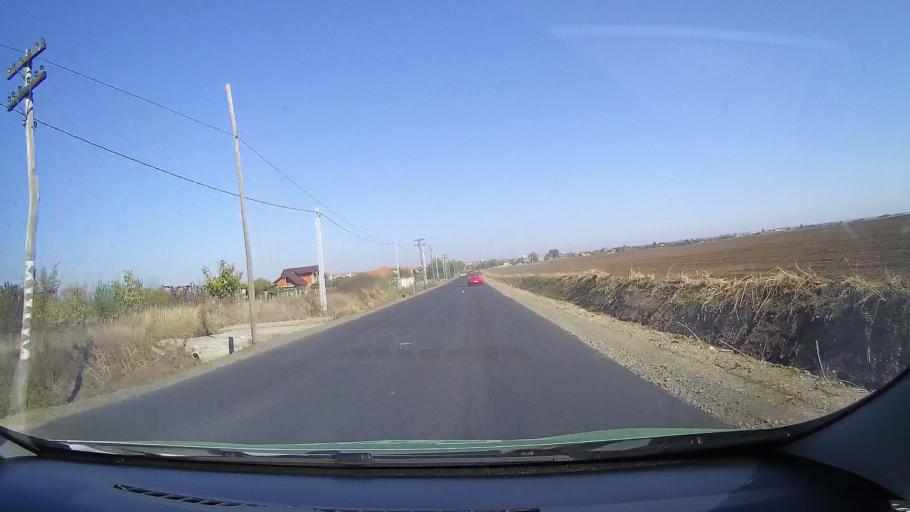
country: RO
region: Satu Mare
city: Carei
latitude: 47.6631
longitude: 22.4606
